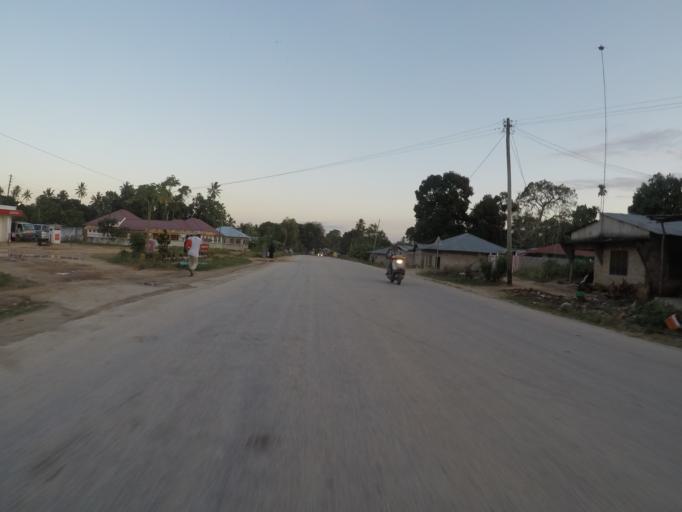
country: TZ
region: Zanzibar North
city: Gamba
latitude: -5.9932
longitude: 39.2523
